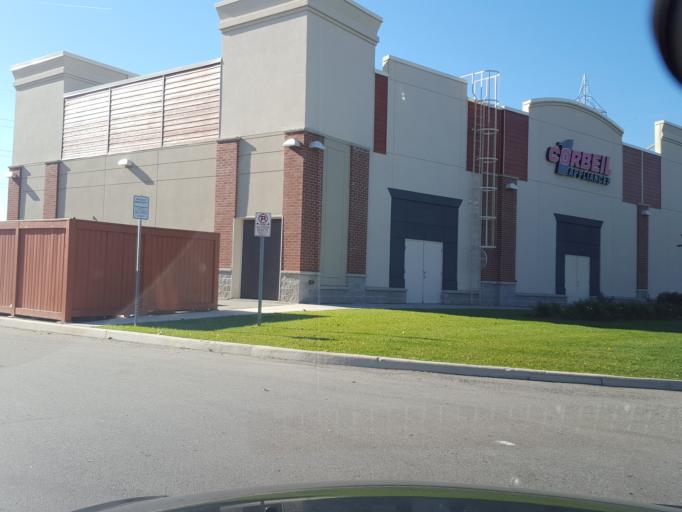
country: CA
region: Ontario
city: Burlington
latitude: 43.3468
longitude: -79.8164
